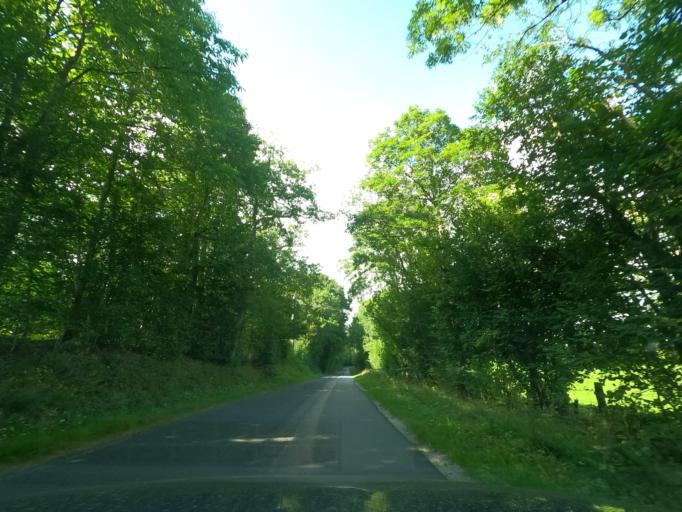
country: FR
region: Lower Normandy
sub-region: Departement de l'Orne
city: Gace
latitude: 48.7786
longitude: 0.2582
